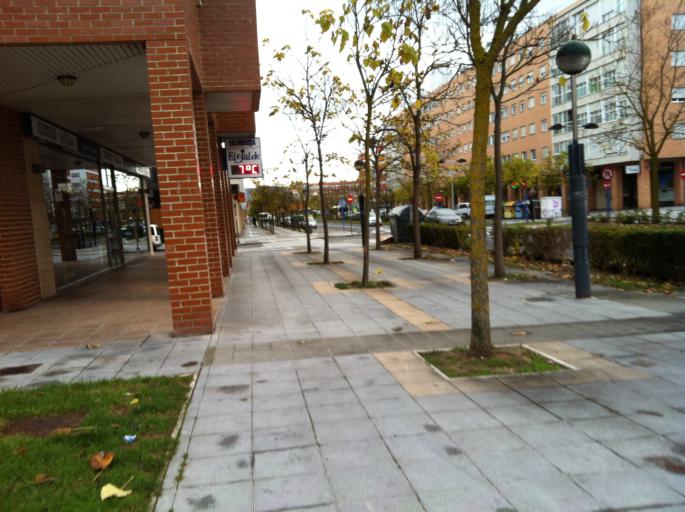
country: ES
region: Basque Country
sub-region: Provincia de Alava
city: Gasteiz / Vitoria
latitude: 42.8667
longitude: -2.6917
